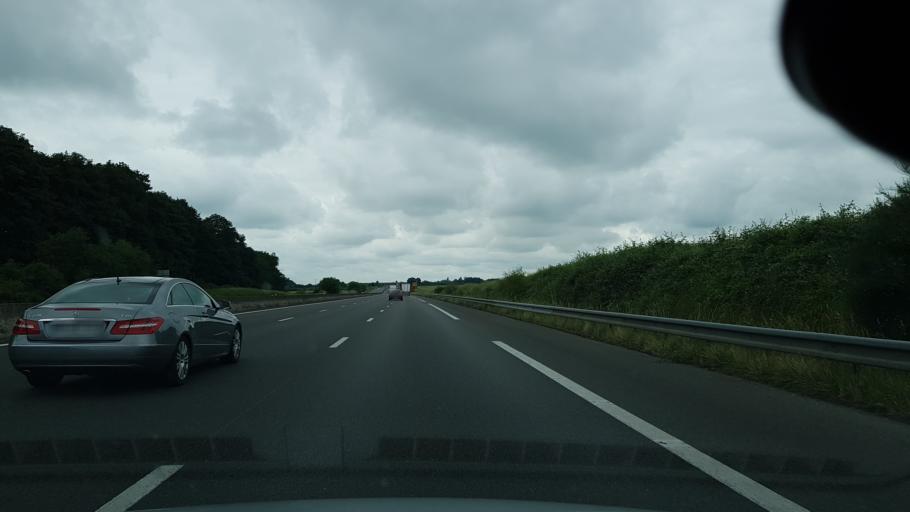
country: FR
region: Centre
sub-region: Departement du Loir-et-Cher
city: Herbault
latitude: 47.5955
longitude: 1.0965
